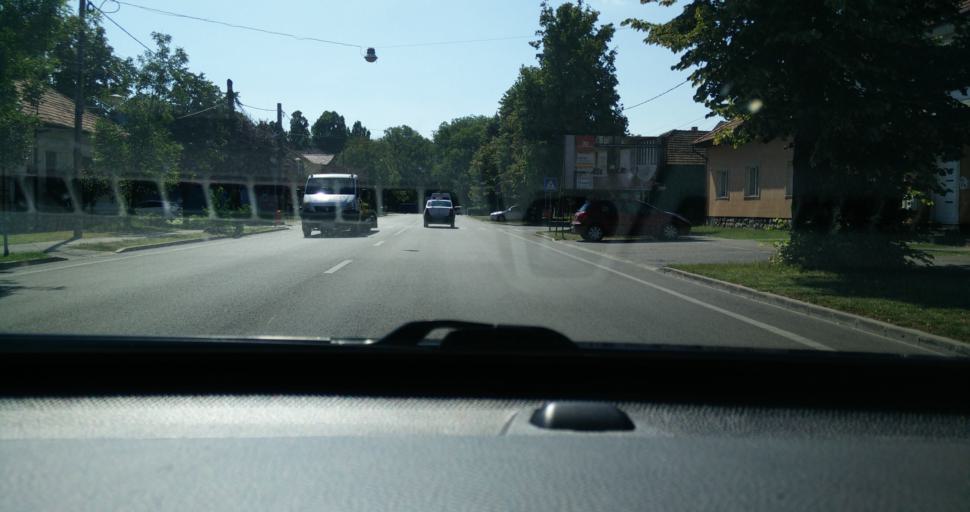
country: RO
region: Bihor
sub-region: Comuna Biharea
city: Oradea
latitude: 47.0454
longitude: 21.9330
